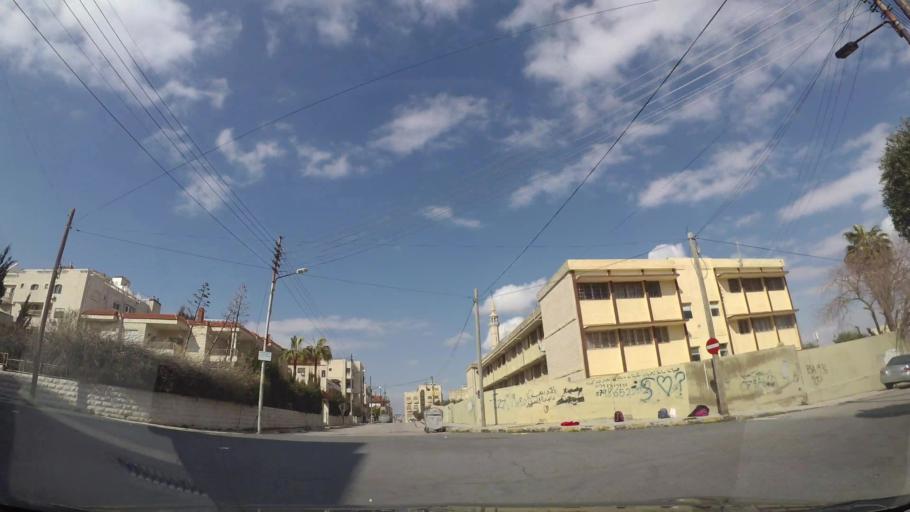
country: JO
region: Amman
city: Amman
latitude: 31.9734
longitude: 35.8919
